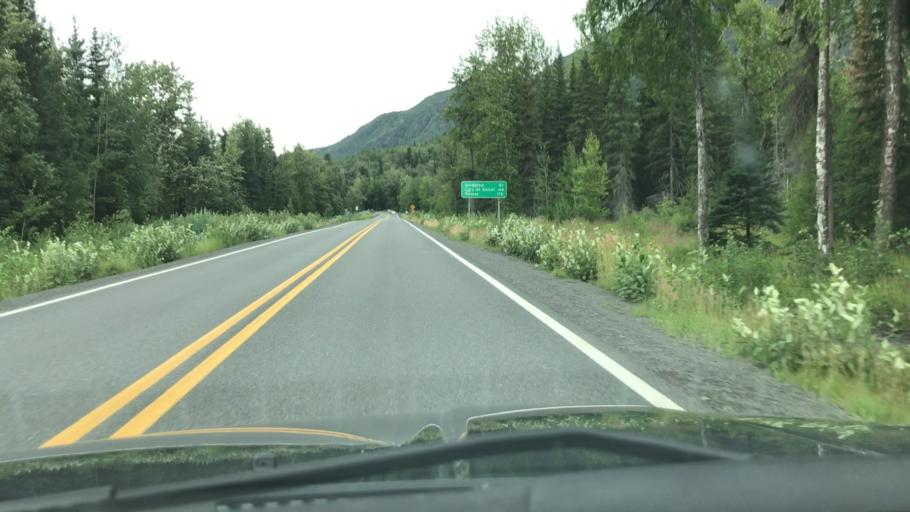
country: US
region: Alaska
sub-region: Kenai Peninsula Borough
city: Seward
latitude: 60.4871
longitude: -149.9704
